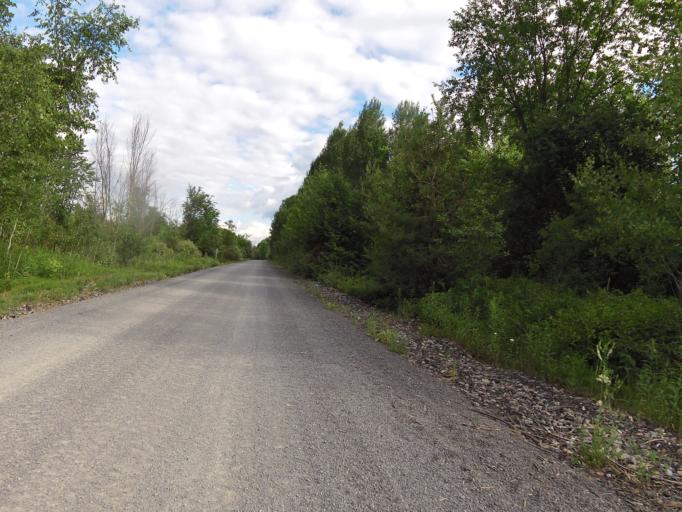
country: CA
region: Ontario
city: Arnprior
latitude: 45.2985
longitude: -76.2634
